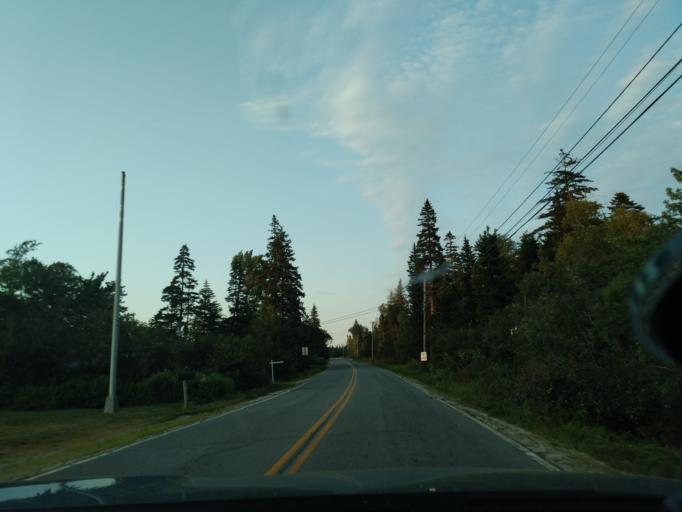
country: US
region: Maine
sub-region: Hancock County
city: Gouldsboro
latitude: 44.3683
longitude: -68.0372
